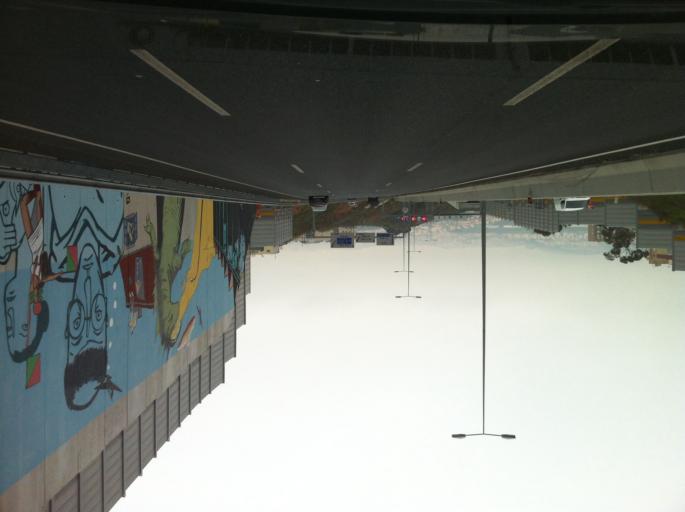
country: PT
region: Lisbon
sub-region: Odivelas
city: Pontinha
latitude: 38.7624
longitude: -9.2020
